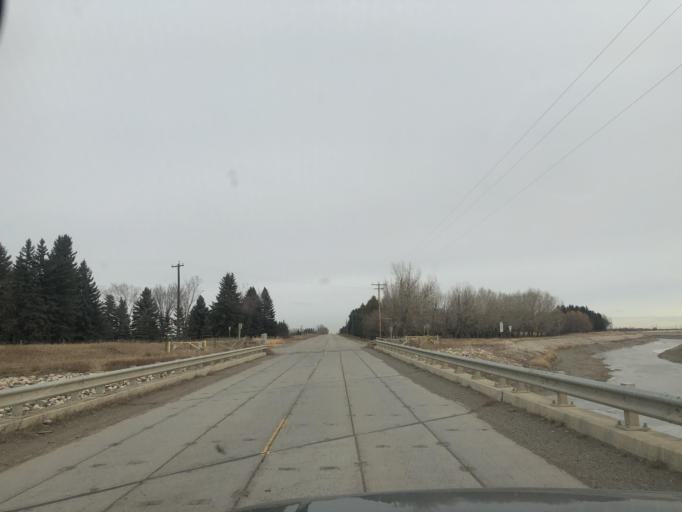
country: CA
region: Alberta
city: Chestermere
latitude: 50.9888
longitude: -113.8654
